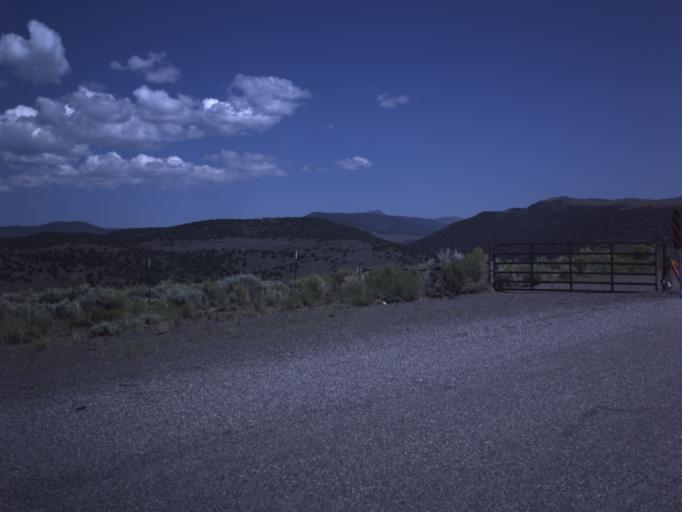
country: US
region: Utah
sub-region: Wayne County
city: Loa
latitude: 38.5111
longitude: -111.5260
